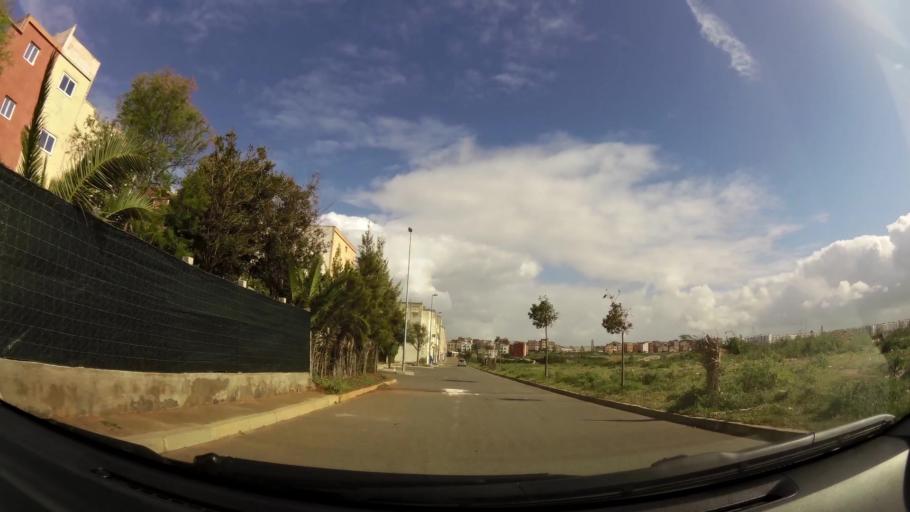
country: MA
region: Grand Casablanca
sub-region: Casablanca
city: Casablanca
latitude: 33.5665
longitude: -7.6986
